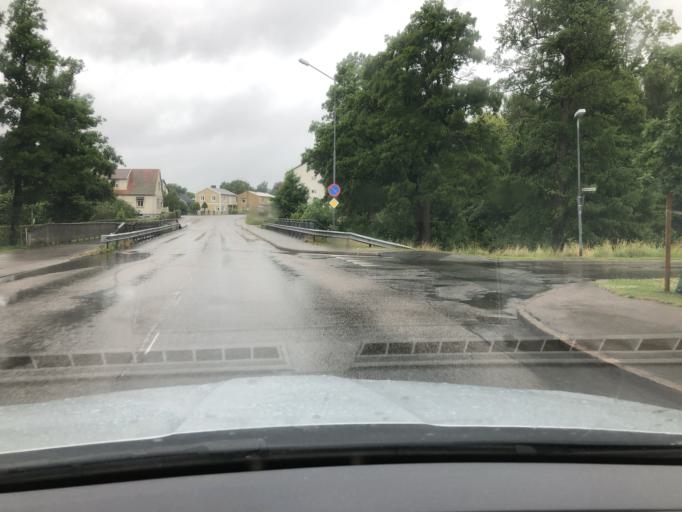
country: SE
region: Blekinge
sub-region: Olofstroms Kommun
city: Olofstroem
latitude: 56.2787
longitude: 14.5308
